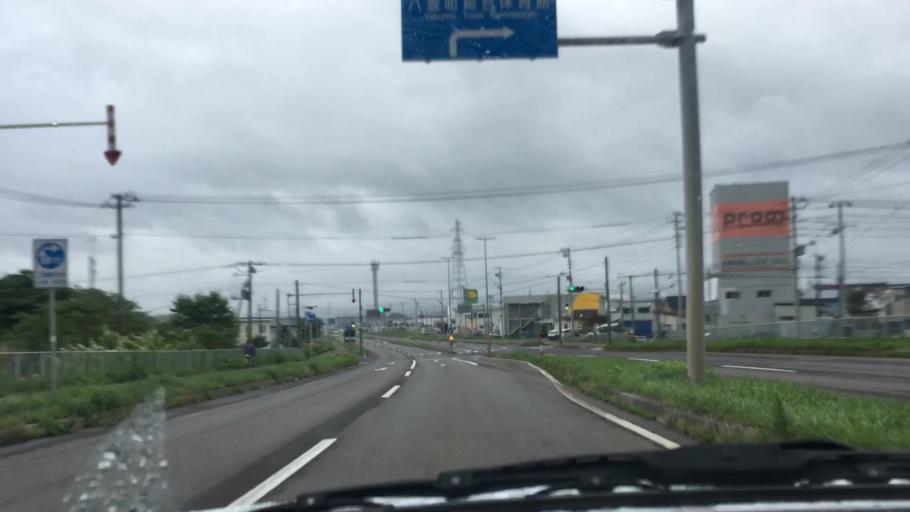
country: JP
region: Hokkaido
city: Nanae
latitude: 42.2620
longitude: 140.2744
